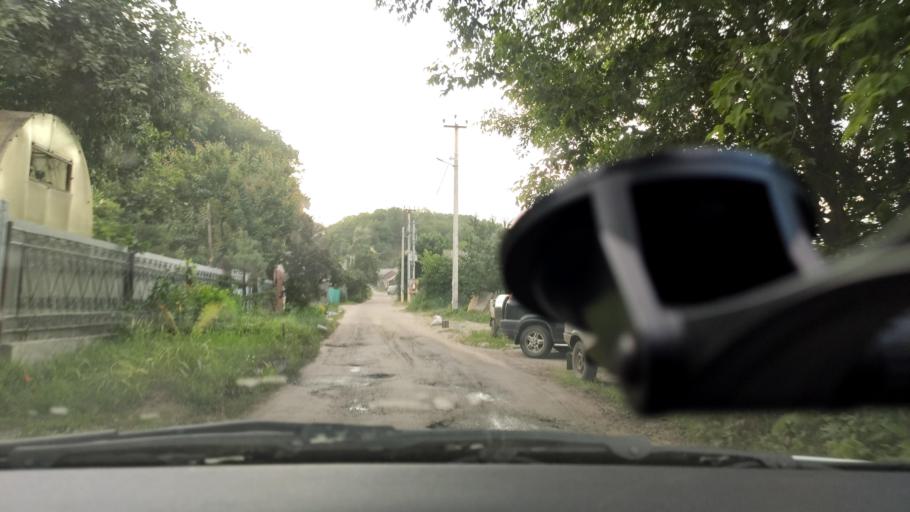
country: RU
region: Voronezj
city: Ramon'
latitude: 51.8939
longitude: 39.3426
